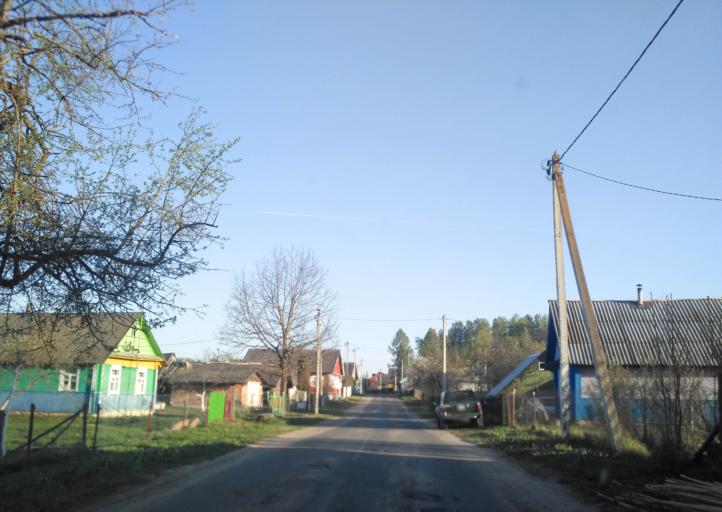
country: BY
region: Minsk
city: Pyatryshki
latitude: 54.1021
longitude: 27.1934
